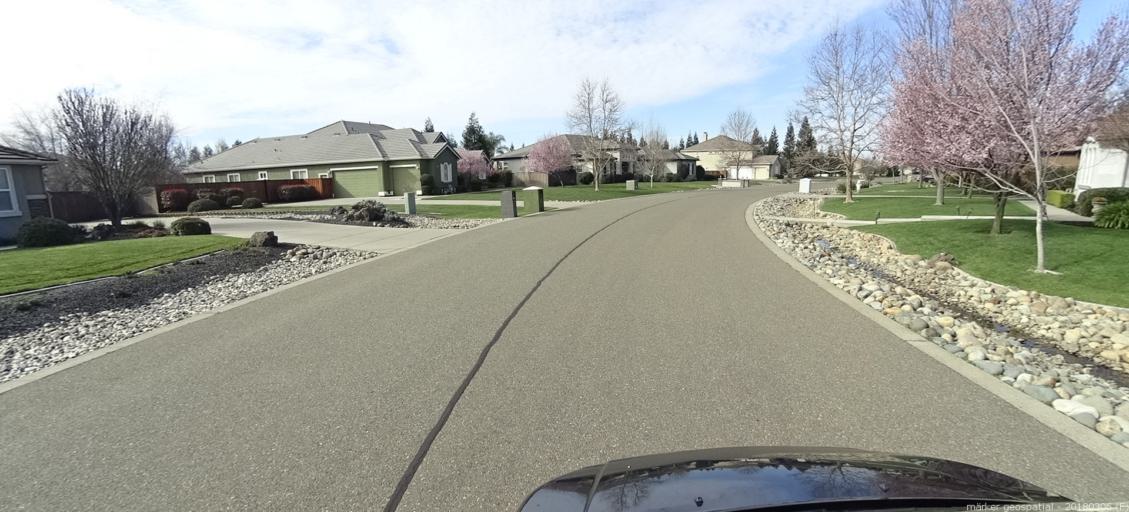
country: US
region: California
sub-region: Sacramento County
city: Vineyard
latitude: 38.4650
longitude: -121.3077
